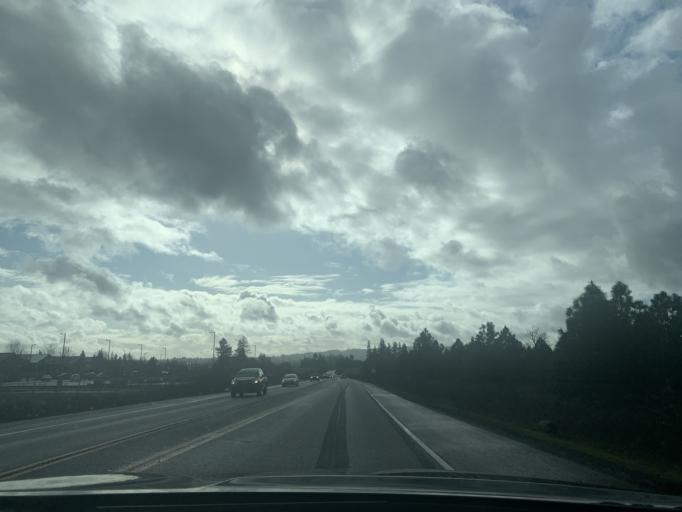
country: US
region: Oregon
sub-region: Washington County
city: Sherwood
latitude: 45.3988
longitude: -122.8519
